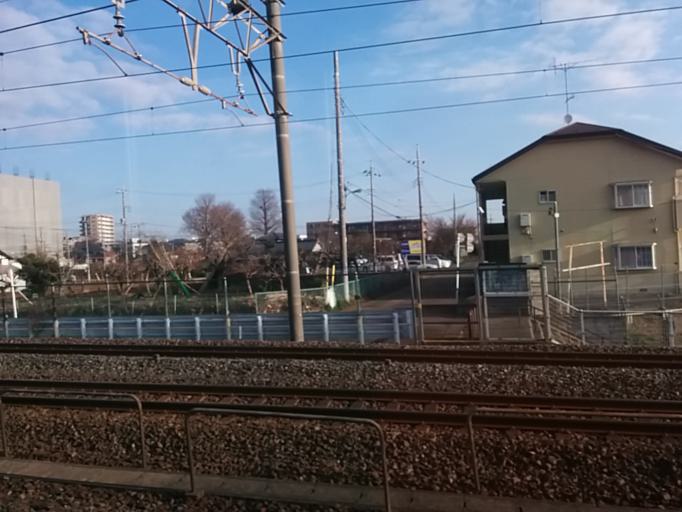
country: JP
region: Saitama
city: Asaka
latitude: 35.8132
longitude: 139.5889
